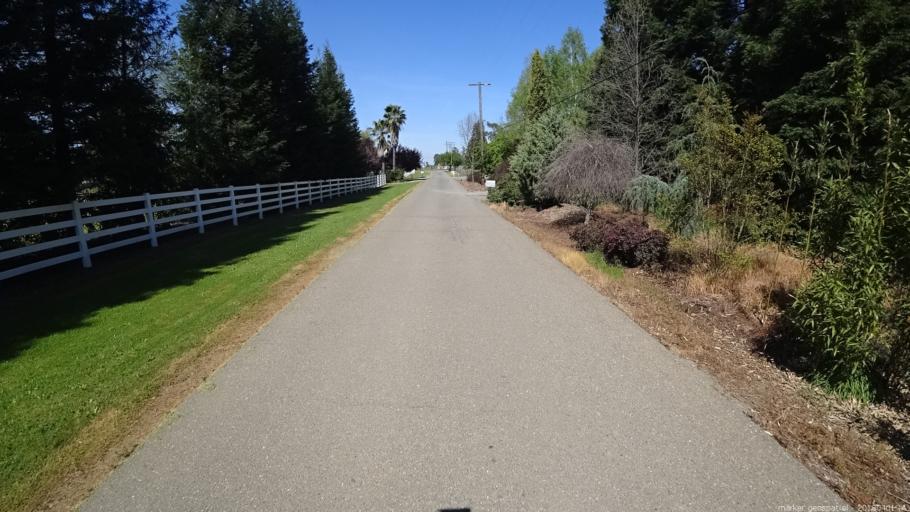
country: US
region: California
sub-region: Sacramento County
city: Wilton
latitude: 38.3855
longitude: -121.2193
